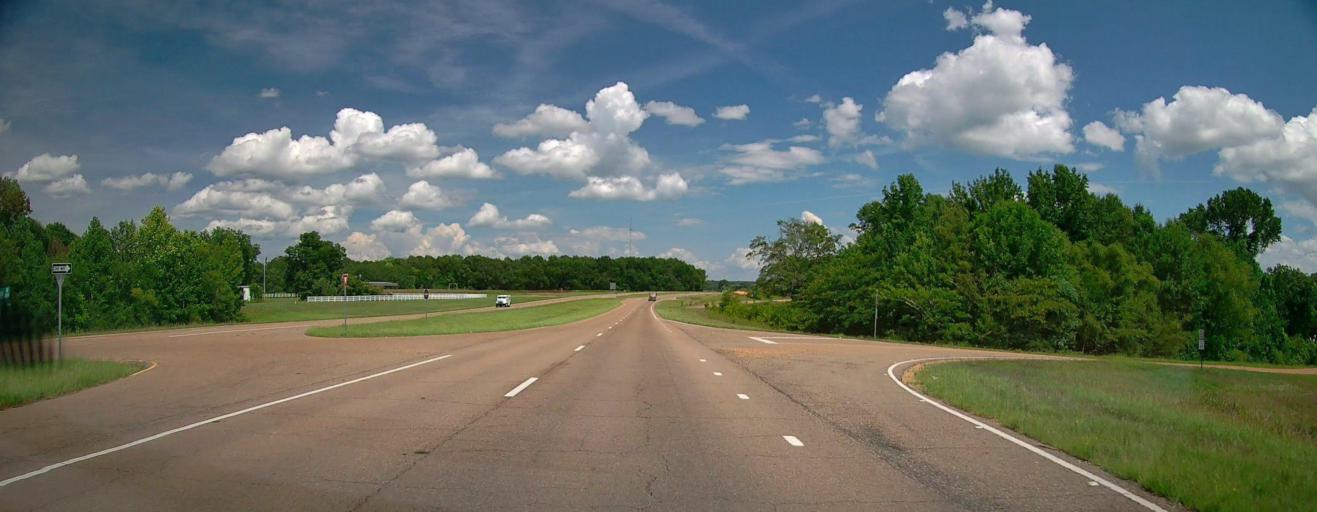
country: US
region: Mississippi
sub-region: Monroe County
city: Aberdeen
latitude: 33.8079
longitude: -88.4763
